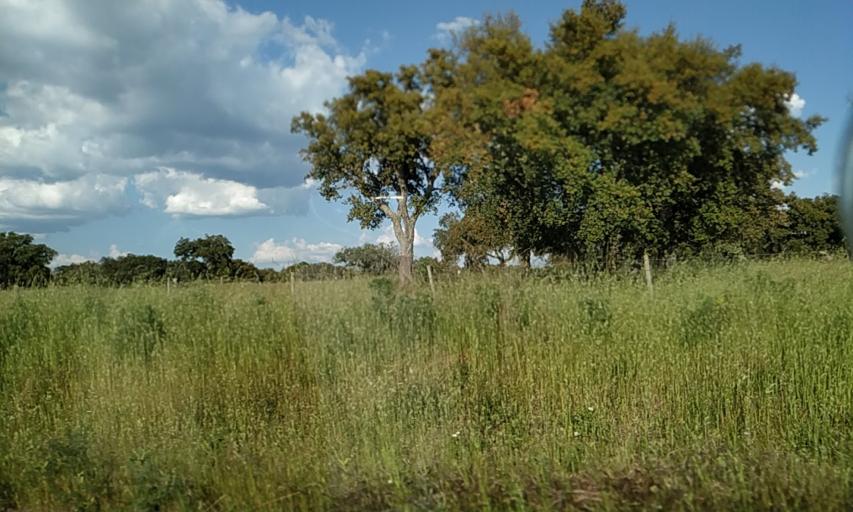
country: PT
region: Portalegre
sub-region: Portalegre
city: Urra
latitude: 39.1675
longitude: -7.4538
